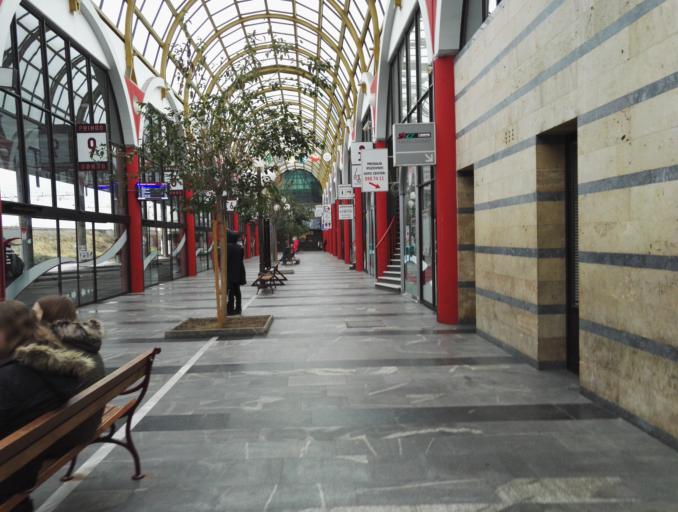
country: SI
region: Maribor
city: Maribor
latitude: 46.5604
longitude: 15.6560
